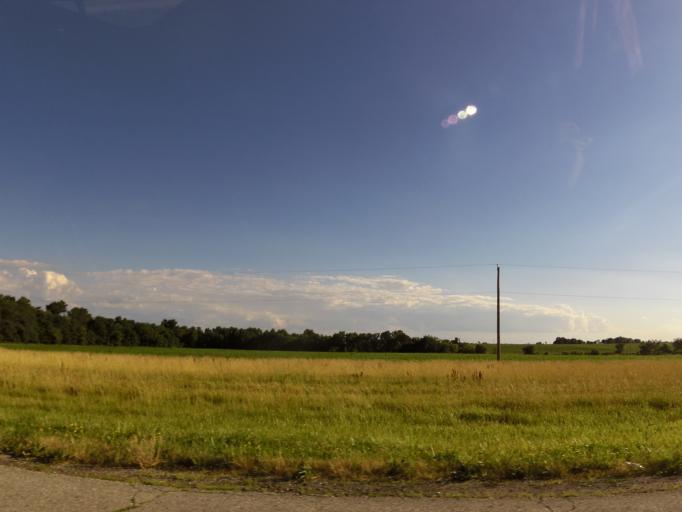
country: US
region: Missouri
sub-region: Pike County
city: Bowling Green
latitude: 39.3170
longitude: -91.1452
